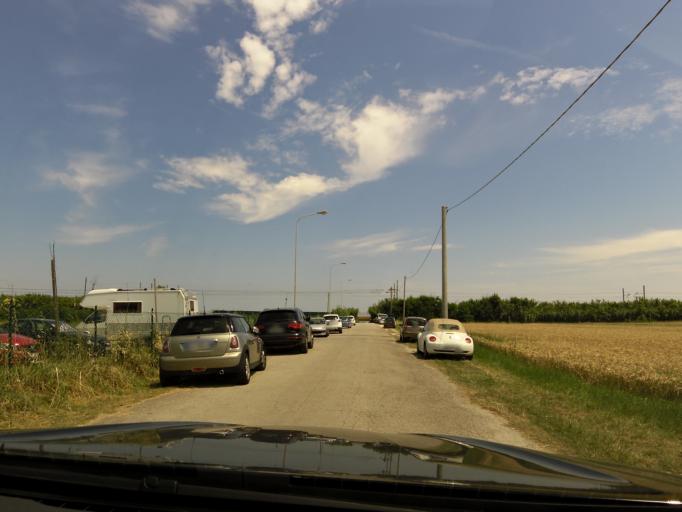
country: IT
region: The Marches
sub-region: Provincia di Pesaro e Urbino
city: Marotta
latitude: 43.8177
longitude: 13.0698
